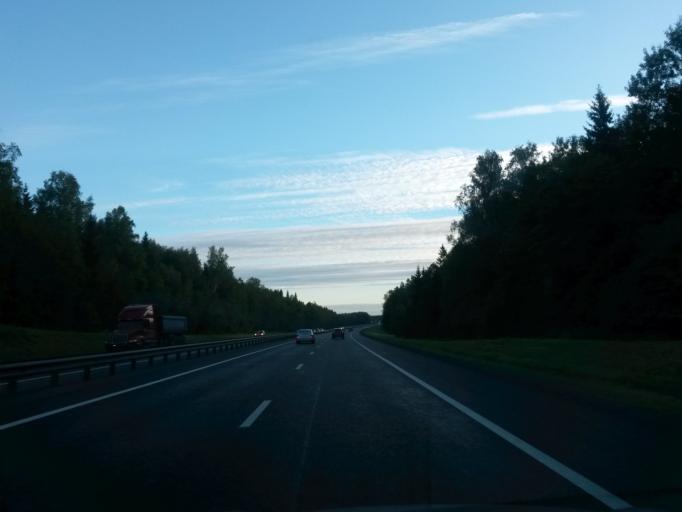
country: RU
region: Moskovskaya
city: Svatkovo
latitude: 56.4117
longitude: 38.3287
